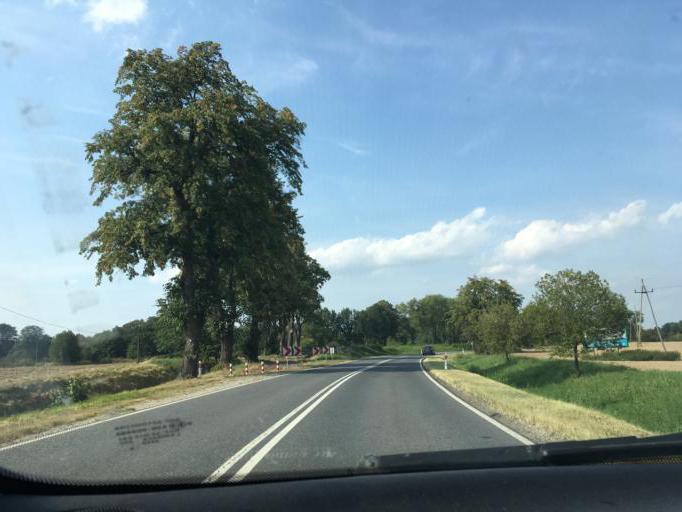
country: PL
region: Opole Voivodeship
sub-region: Powiat prudnicki
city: Laka Prudnicka
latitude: 50.3977
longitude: 17.5081
